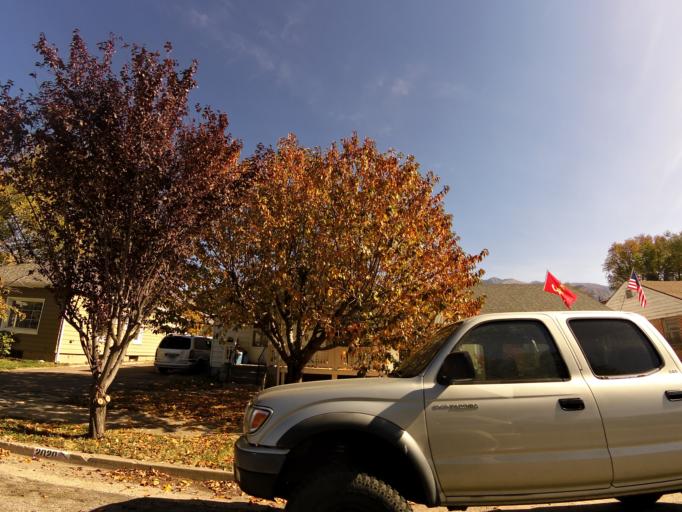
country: US
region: Utah
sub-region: Weber County
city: Ogden
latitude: 41.2305
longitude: -111.9605
